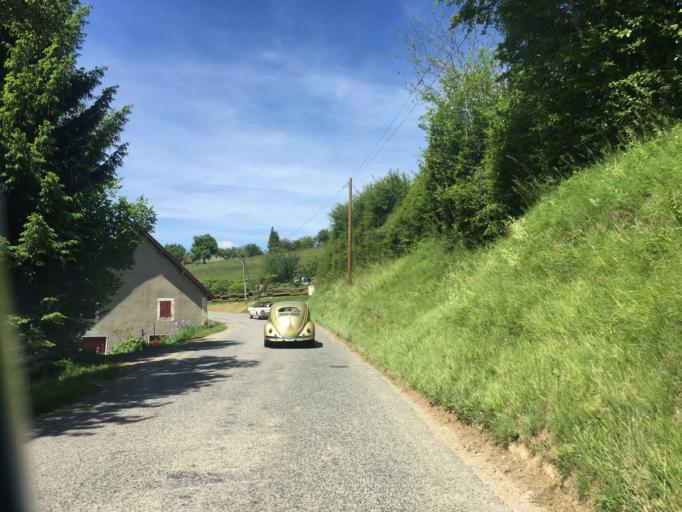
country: FR
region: Rhone-Alpes
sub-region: Departement de la Haute-Savoie
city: Vallieres
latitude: 45.9319
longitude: 5.9759
